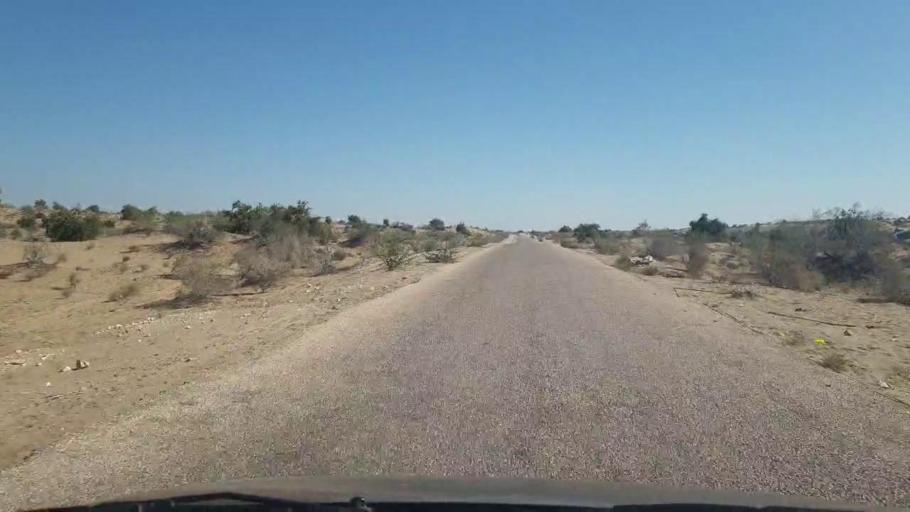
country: PK
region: Sindh
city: Bozdar
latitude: 27.0053
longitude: 68.8752
